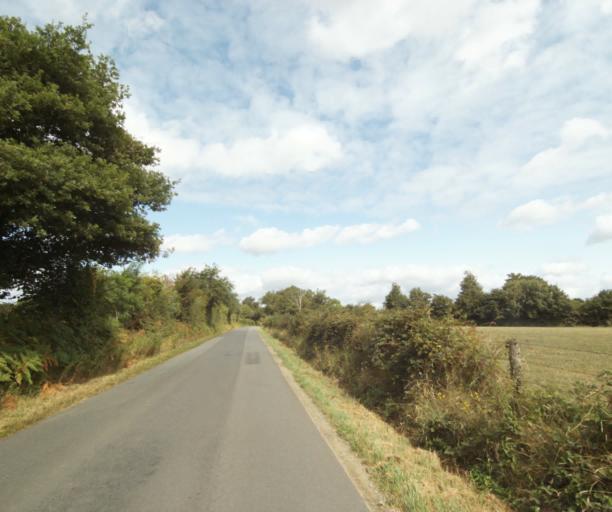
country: FR
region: Pays de la Loire
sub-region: Departement de la Sarthe
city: Sable-sur-Sarthe
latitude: 47.8105
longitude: -0.3137
